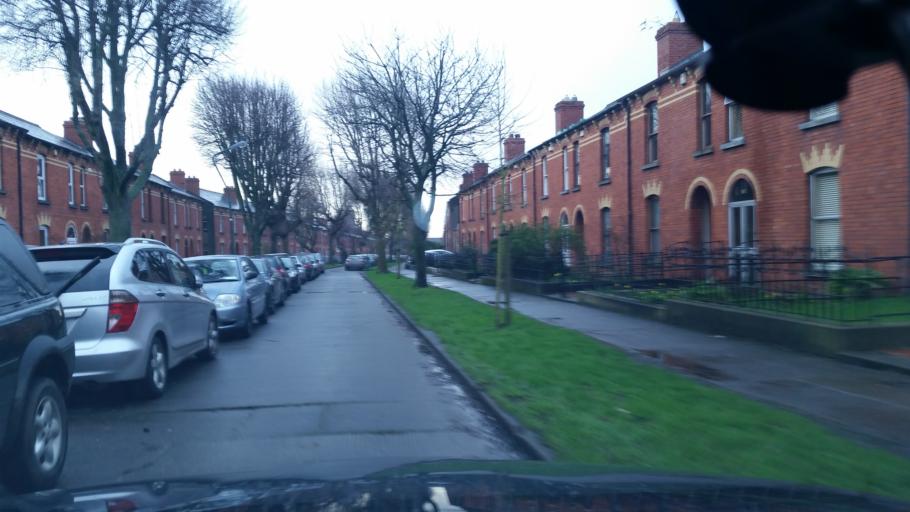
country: IE
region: Leinster
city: Cabra
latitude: 53.3657
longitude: -6.2805
